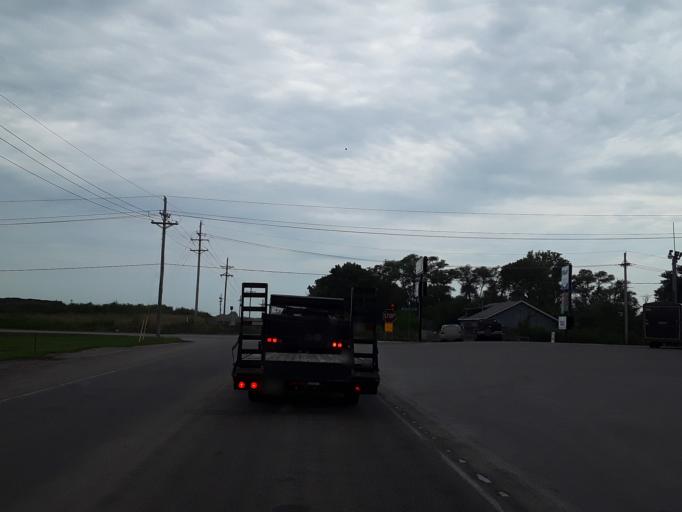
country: US
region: Nebraska
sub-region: Saunders County
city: Yutan
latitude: 41.2346
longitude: -96.3304
